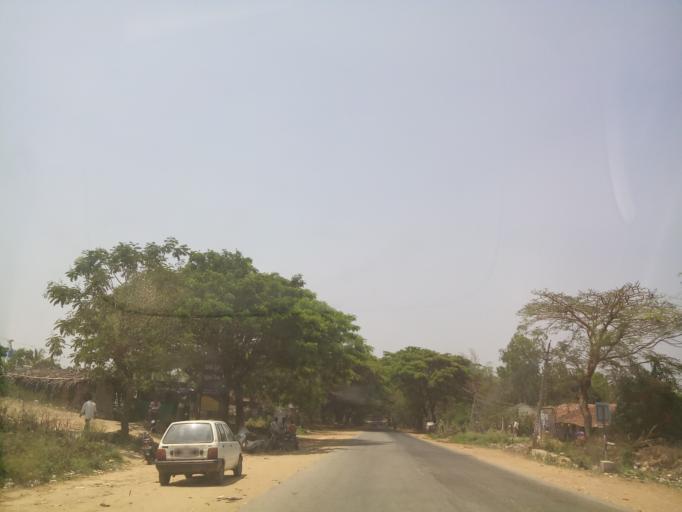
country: IN
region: Karnataka
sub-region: Hassan
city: Hassan
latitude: 12.9880
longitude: 76.0472
